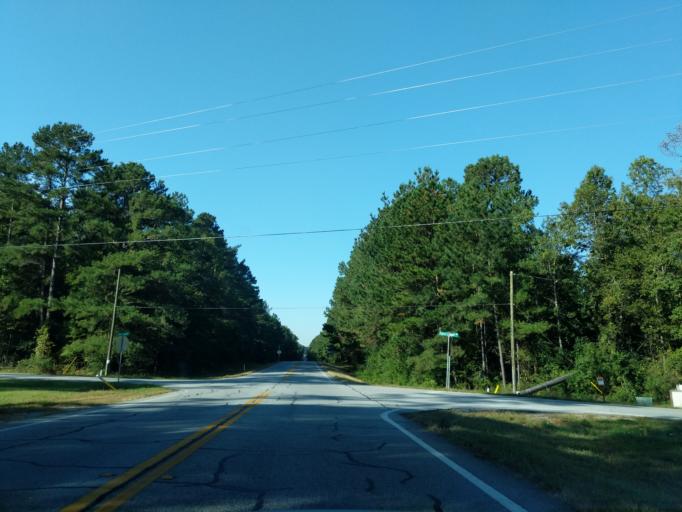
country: US
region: Georgia
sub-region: Coweta County
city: Newnan
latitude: 33.3515
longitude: -84.9181
